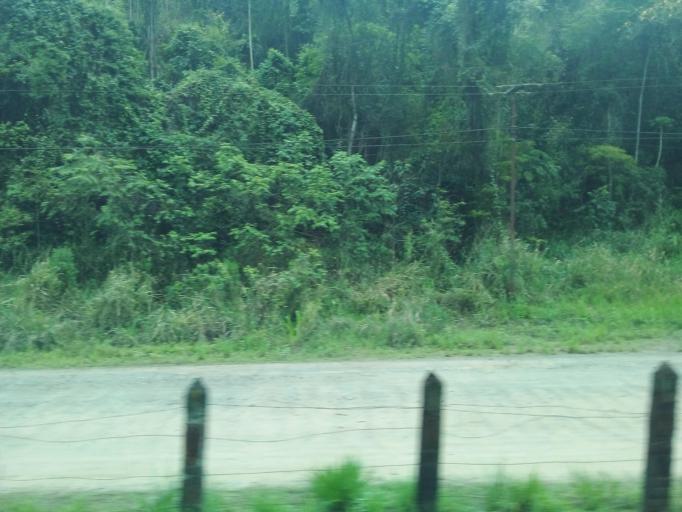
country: BR
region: Minas Gerais
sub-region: Nova Era
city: Nova Era
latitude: -19.7245
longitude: -42.9885
